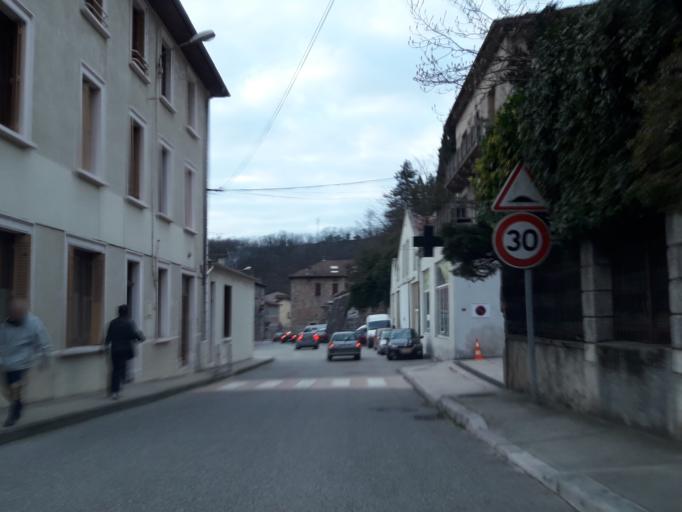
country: FR
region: Rhone-Alpes
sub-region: Departement de l'Isere
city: Pont-en-Royans
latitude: 45.0620
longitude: 5.3427
